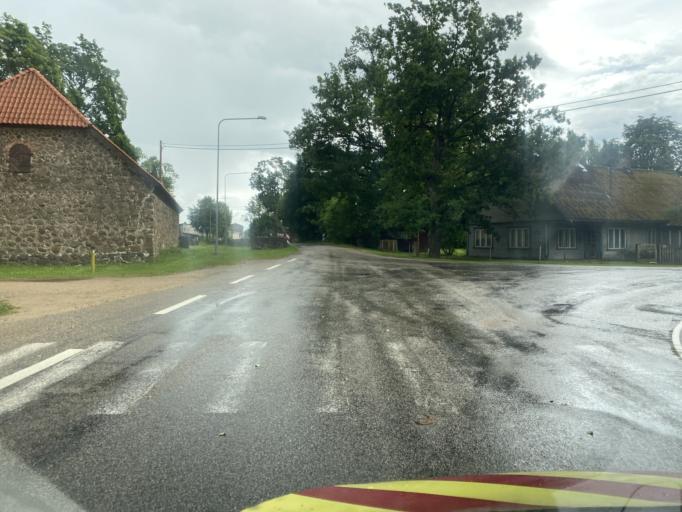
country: EE
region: Valgamaa
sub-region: Torva linn
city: Torva
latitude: 58.0958
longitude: 25.8955
